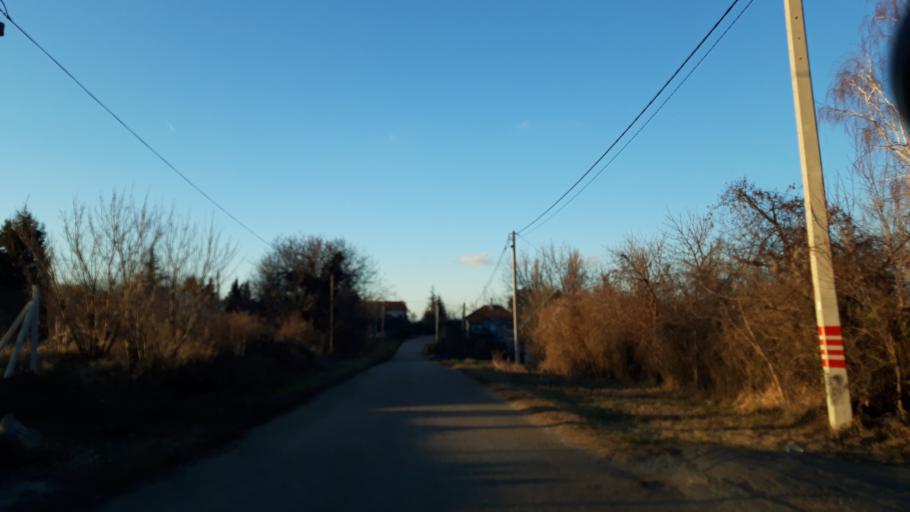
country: RS
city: Cortanovci
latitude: 45.1629
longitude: 20.0010
